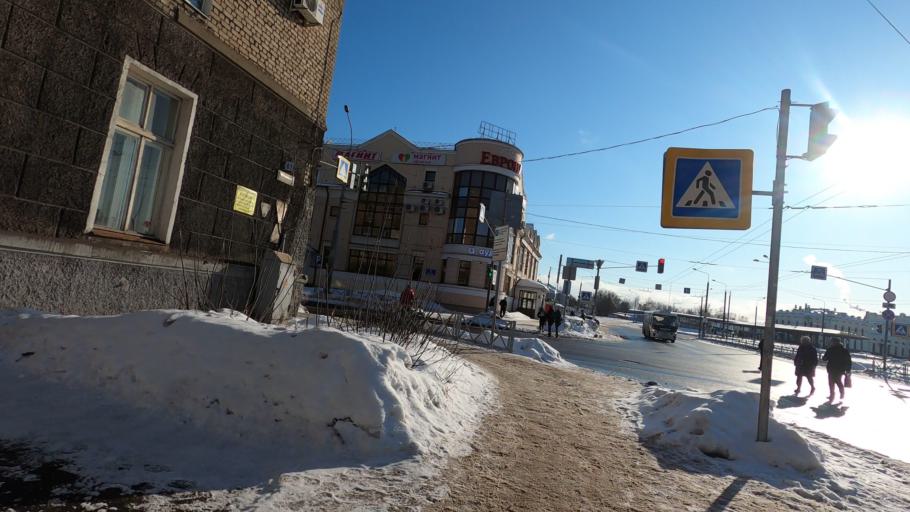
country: RU
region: Jaroslavl
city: Rybinsk
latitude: 58.0434
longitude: 38.8369
